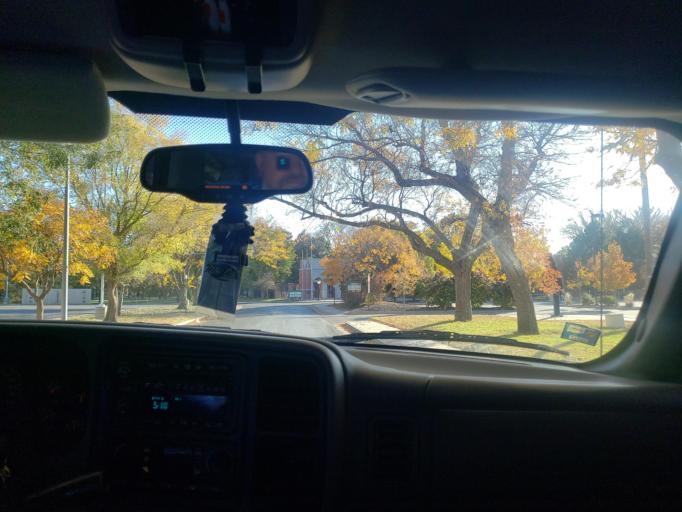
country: US
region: Kansas
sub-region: Finney County
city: Garden City
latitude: 37.9612
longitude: -100.8702
